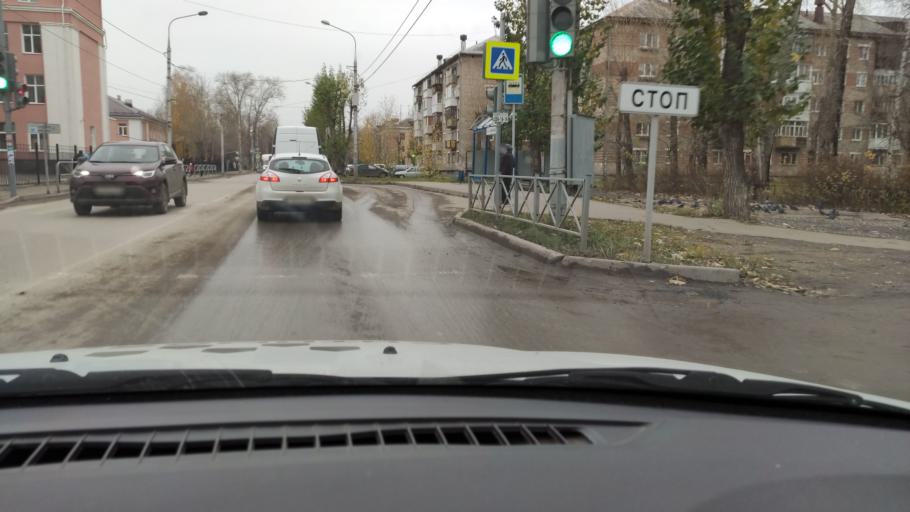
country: RU
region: Perm
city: Perm
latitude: 57.9665
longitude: 56.2354
